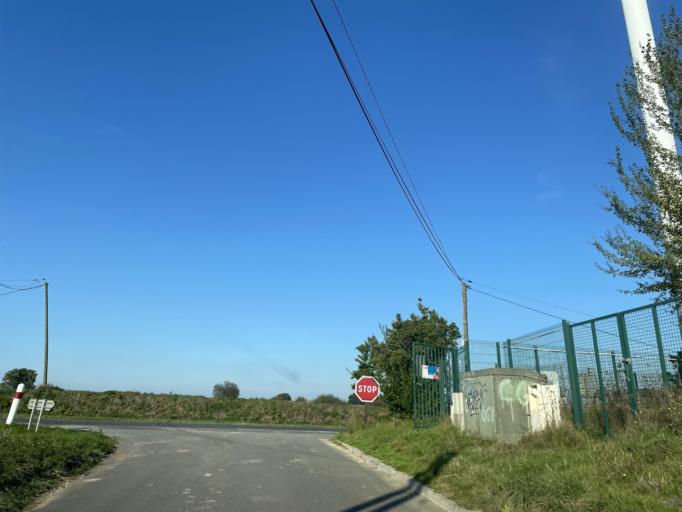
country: FR
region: Ile-de-France
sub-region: Departement de Seine-et-Marne
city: Chailly-en-Brie
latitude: 48.7877
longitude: 3.1605
